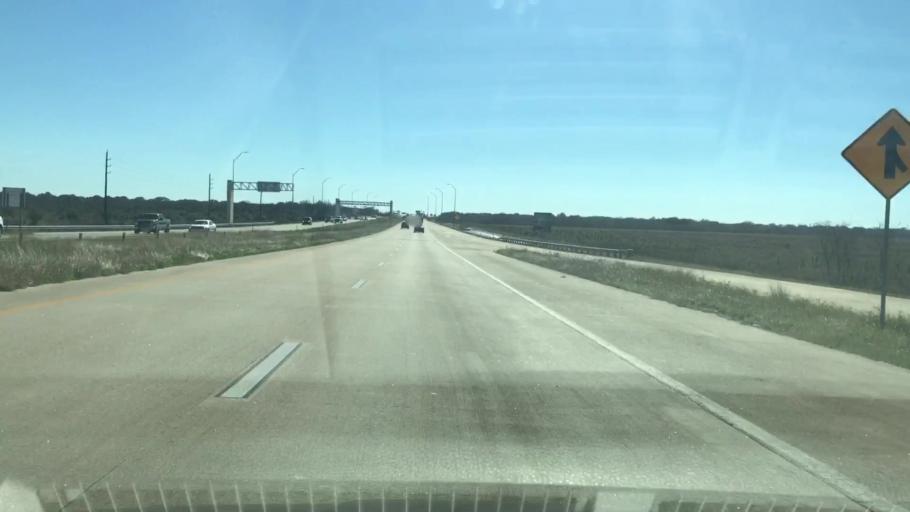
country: US
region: Texas
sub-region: Harris County
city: Cypress
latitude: 29.9743
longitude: -95.7697
